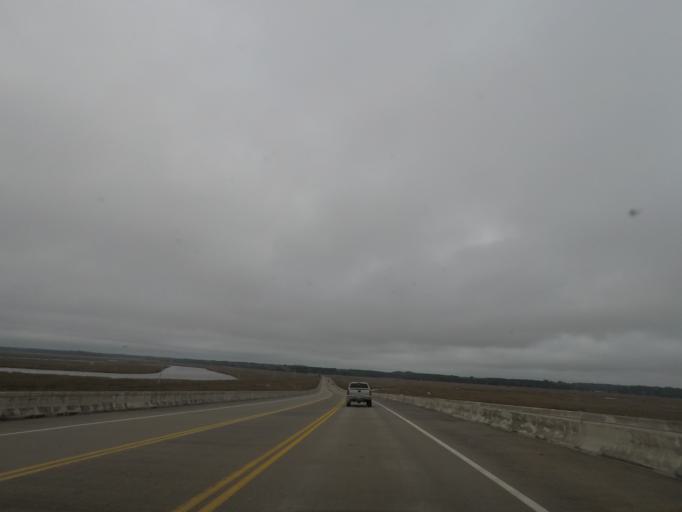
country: US
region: South Carolina
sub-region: Charleston County
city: Meggett
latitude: 32.6394
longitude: -80.3403
